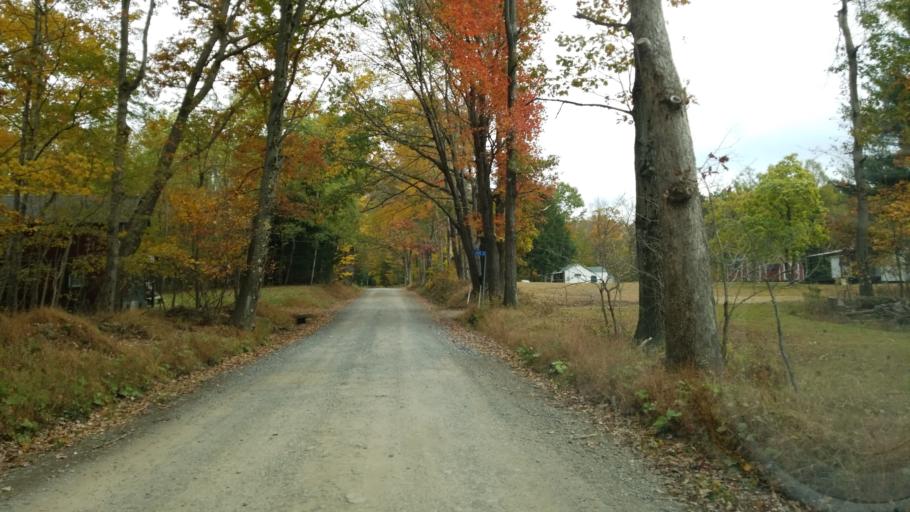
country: US
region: Pennsylvania
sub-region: Clearfield County
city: Shiloh
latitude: 41.1868
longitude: -78.3607
